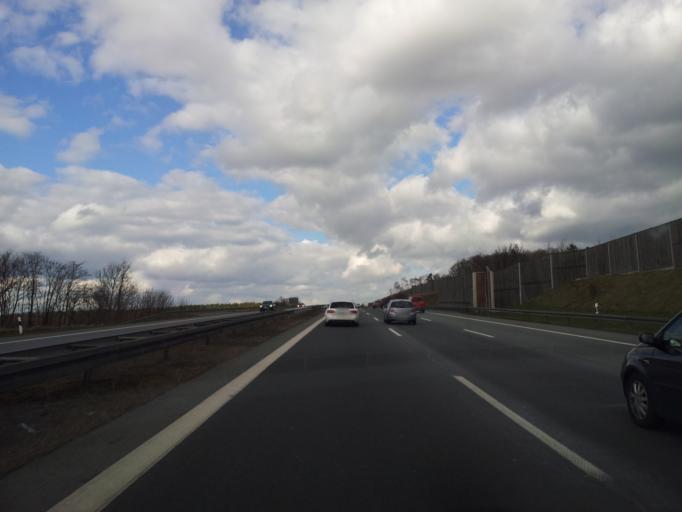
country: DE
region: Saxony
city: Neuensalz
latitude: 50.5274
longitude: 12.2422
